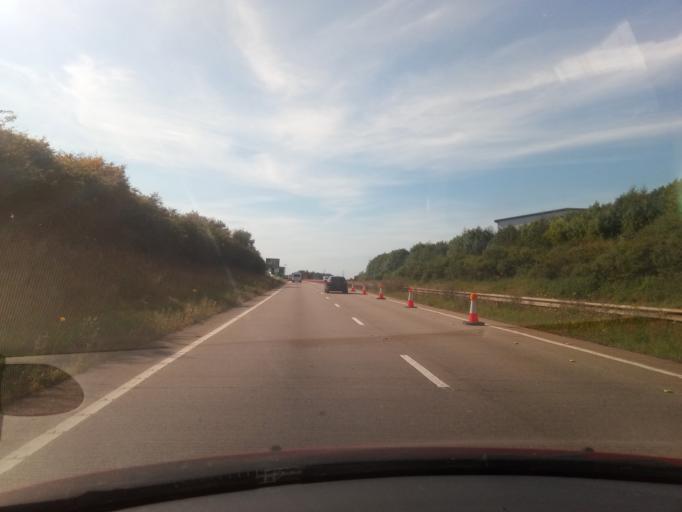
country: GB
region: England
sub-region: Stockton-on-Tees
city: Billingham
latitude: 54.6342
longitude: -1.3028
